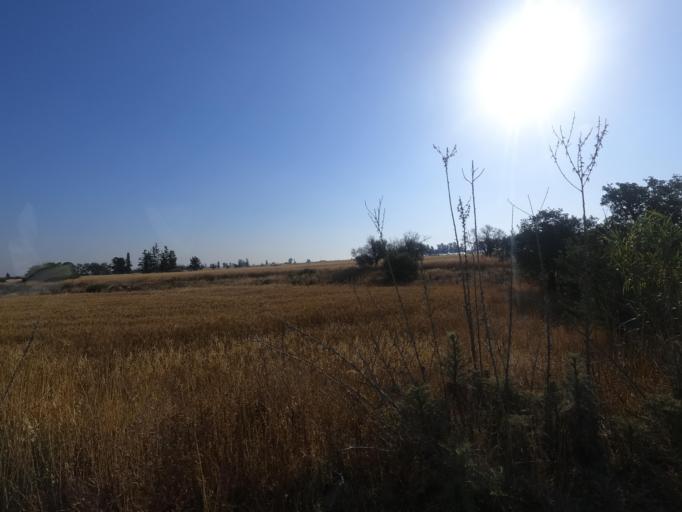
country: CY
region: Ammochostos
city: Frenaros
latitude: 35.0828
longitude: 33.9106
